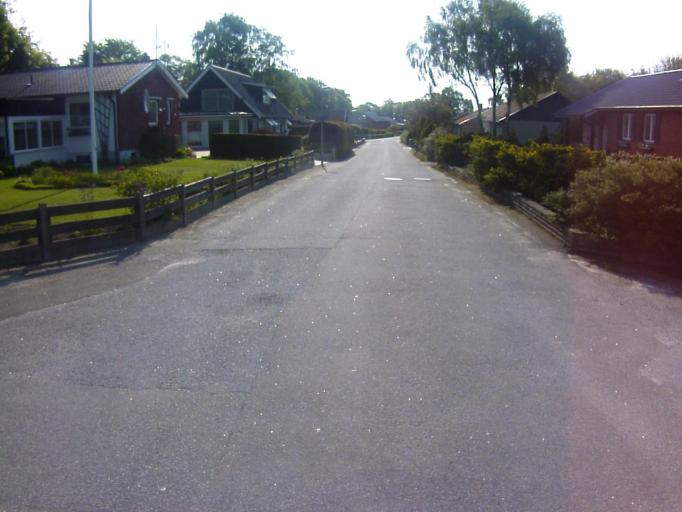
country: SE
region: Blekinge
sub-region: Solvesborgs Kommun
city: Soelvesborg
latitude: 56.0094
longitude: 14.7244
